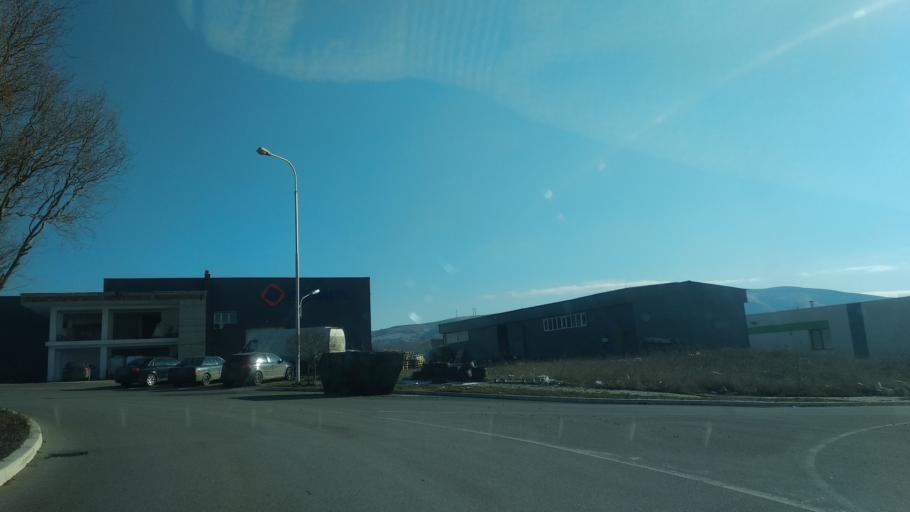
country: XK
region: Pristina
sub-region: Komuna e Drenasit
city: Glogovac
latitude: 42.6019
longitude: 20.9619
